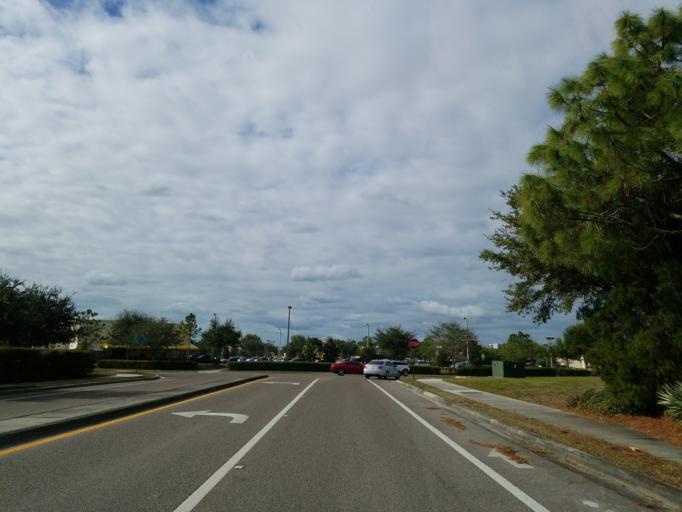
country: US
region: Florida
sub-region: Hillsborough County
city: Progress Village
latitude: 27.9207
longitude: -82.3266
